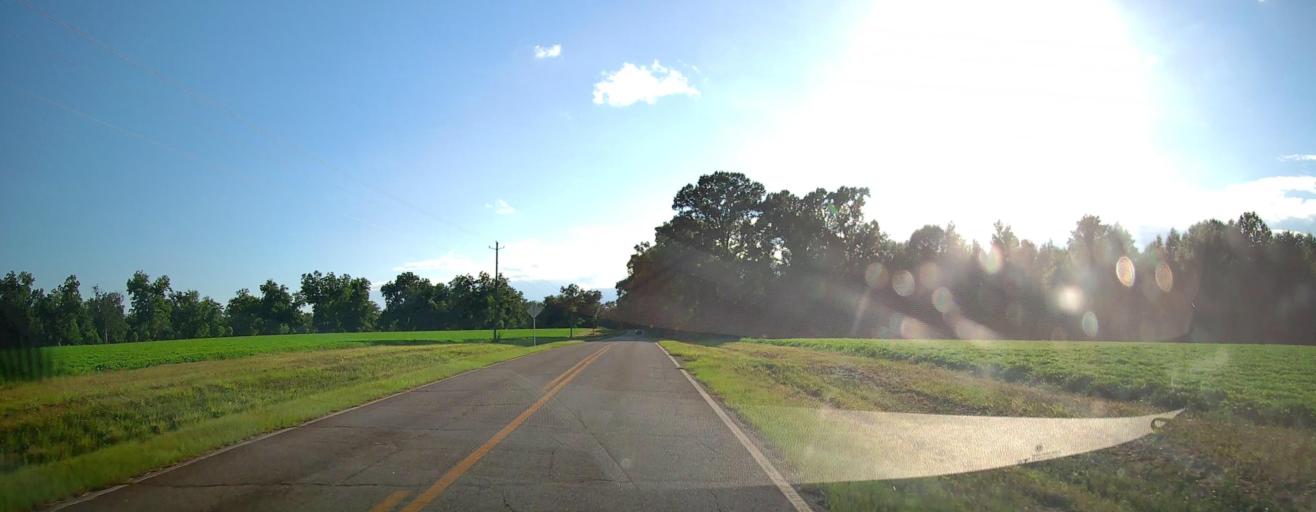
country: US
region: Georgia
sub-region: Bleckley County
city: Cochran
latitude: 32.3916
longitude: -83.4503
